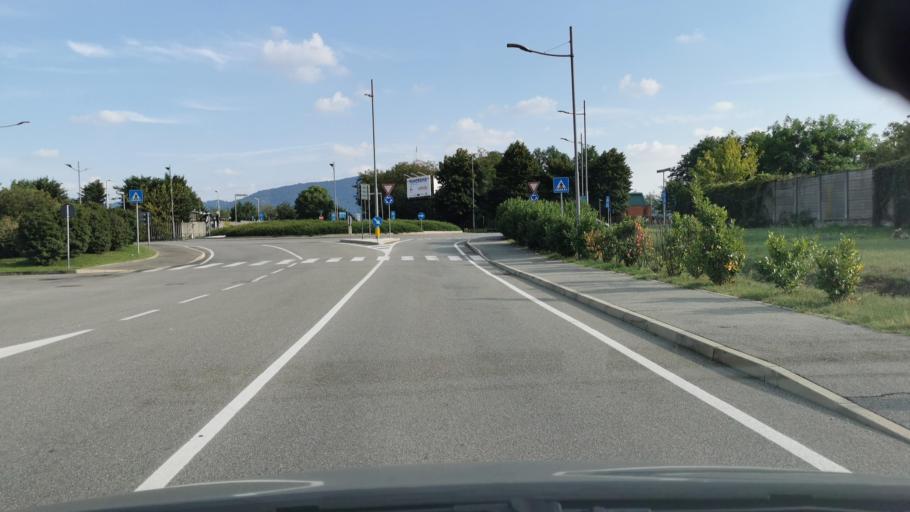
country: IT
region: Piedmont
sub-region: Provincia di Torino
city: Settimo Torinese
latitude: 45.1273
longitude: 7.7360
